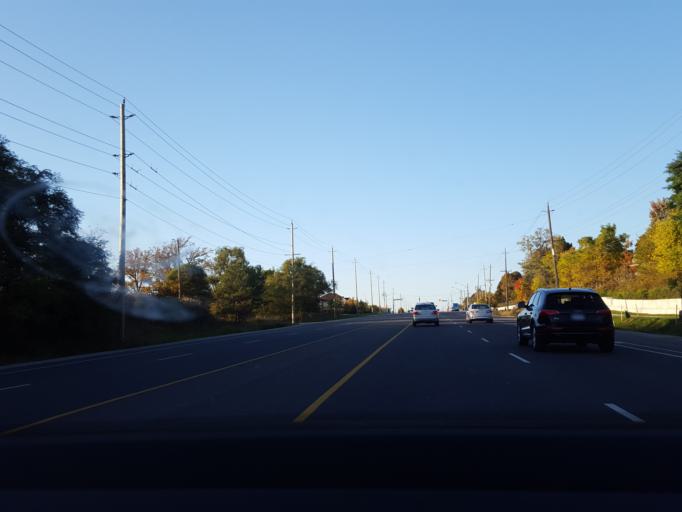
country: CA
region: Ontario
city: Newmarket
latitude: 44.0238
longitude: -79.4732
